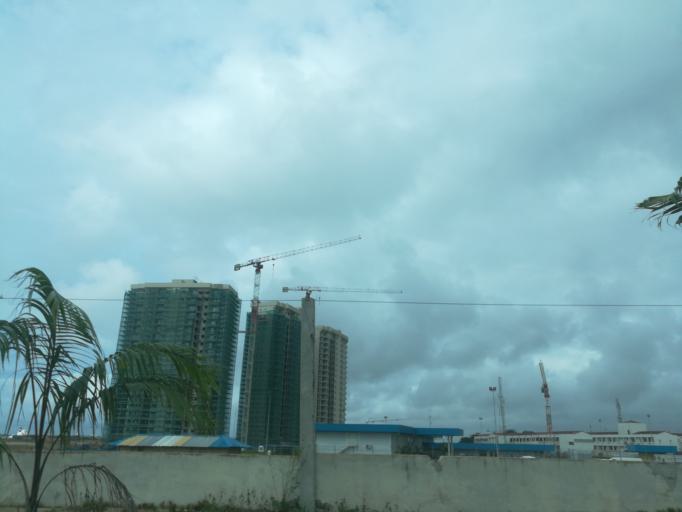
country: NG
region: Lagos
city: Lagos
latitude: 6.4194
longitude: 3.4135
